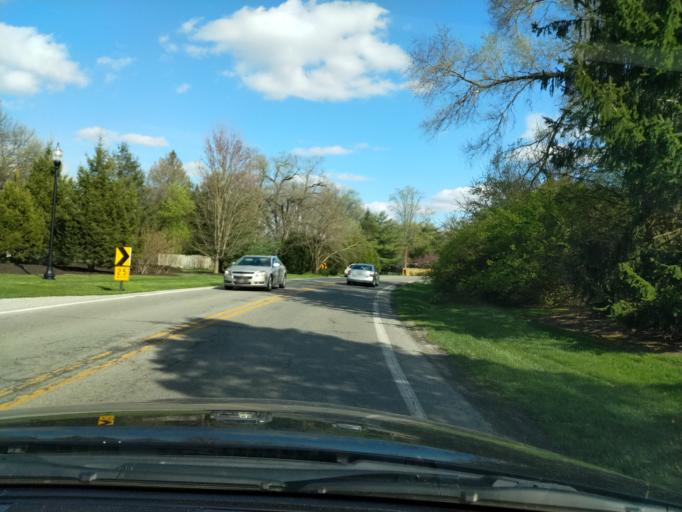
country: US
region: Indiana
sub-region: Marion County
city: Meridian Hills
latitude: 39.8866
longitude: -86.1625
